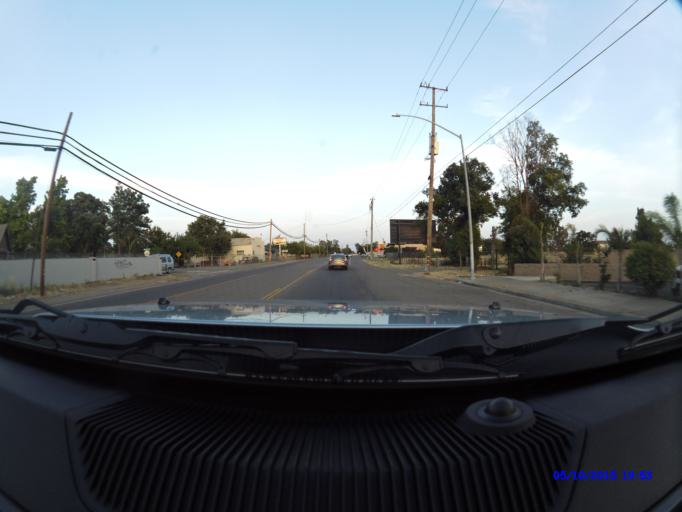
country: US
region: California
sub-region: San Joaquin County
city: Kennedy
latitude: 37.9428
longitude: -121.2519
